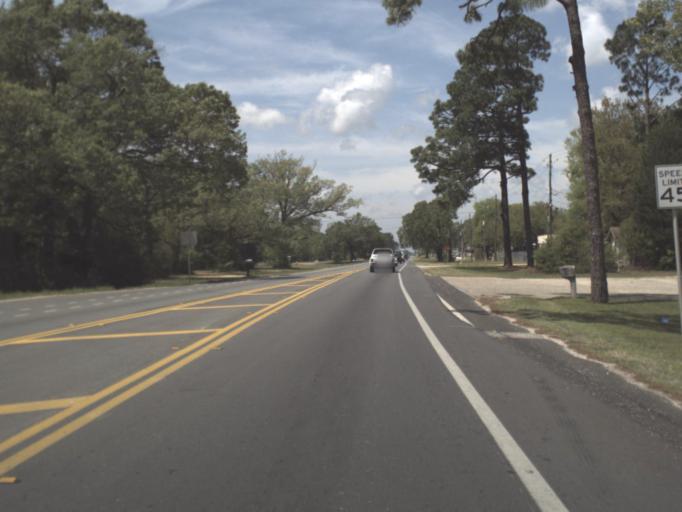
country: US
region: Florida
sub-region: Escambia County
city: Ensley
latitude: 30.5343
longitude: -87.3150
